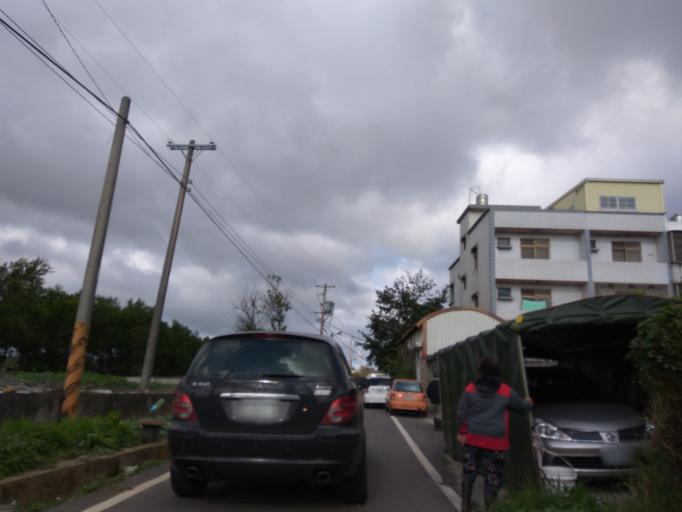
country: TW
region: Taiwan
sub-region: Hsinchu
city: Zhubei
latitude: 24.9737
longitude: 121.0820
